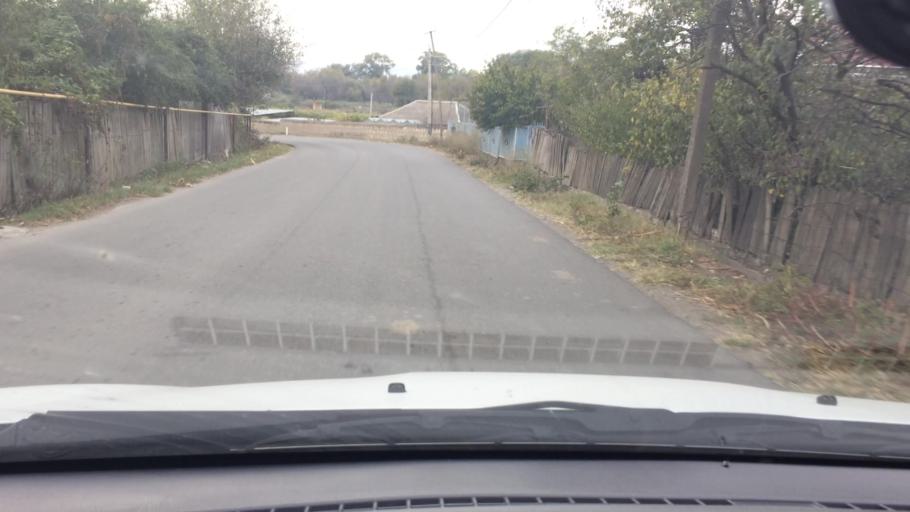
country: AM
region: Tavush
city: Bagratashen
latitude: 41.3407
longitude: 44.8906
